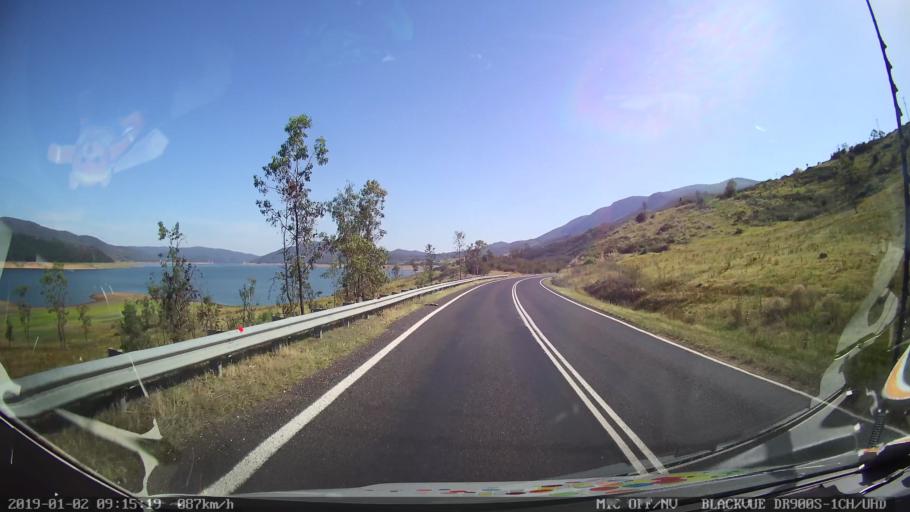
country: AU
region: New South Wales
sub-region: Tumut Shire
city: Tumut
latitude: -35.4664
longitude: 148.2786
